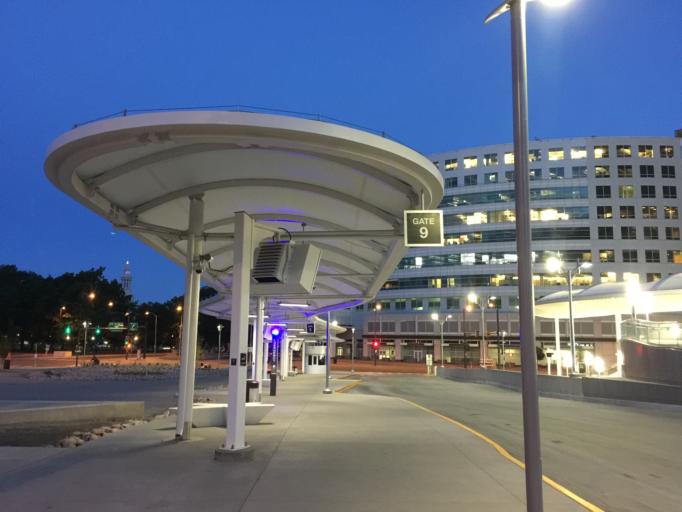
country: US
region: Colorado
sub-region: Denver County
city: Denver
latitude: 39.7406
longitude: -104.9863
